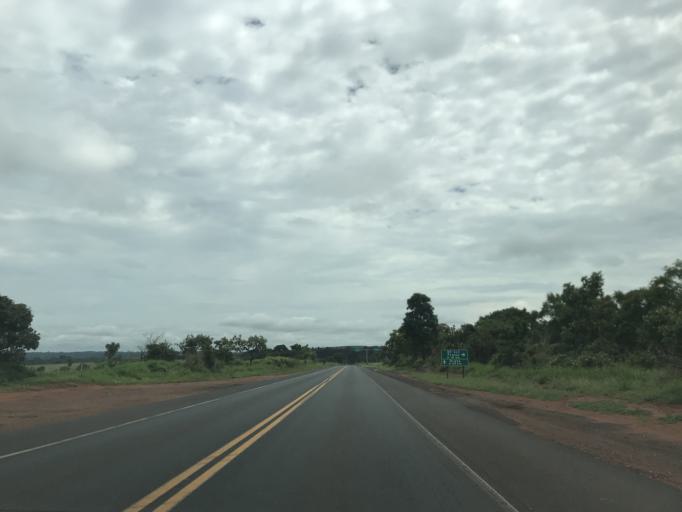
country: BR
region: Minas Gerais
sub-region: Frutal
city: Frutal
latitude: -19.9446
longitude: -48.9638
